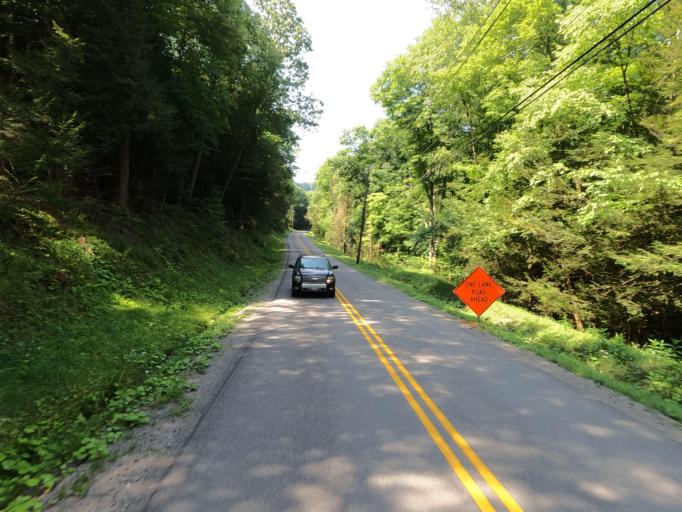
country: US
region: Maryland
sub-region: Garrett County
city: Oakland
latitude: 39.5069
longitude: -79.3908
